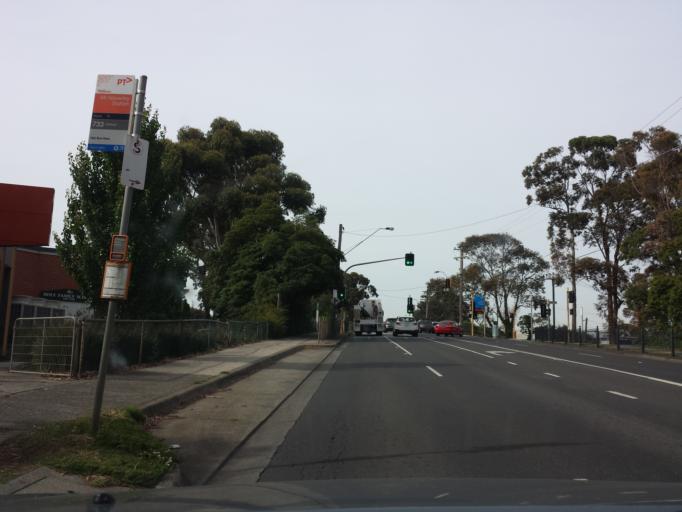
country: AU
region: Victoria
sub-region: Monash
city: Ashwood
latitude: -37.8745
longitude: 145.1293
